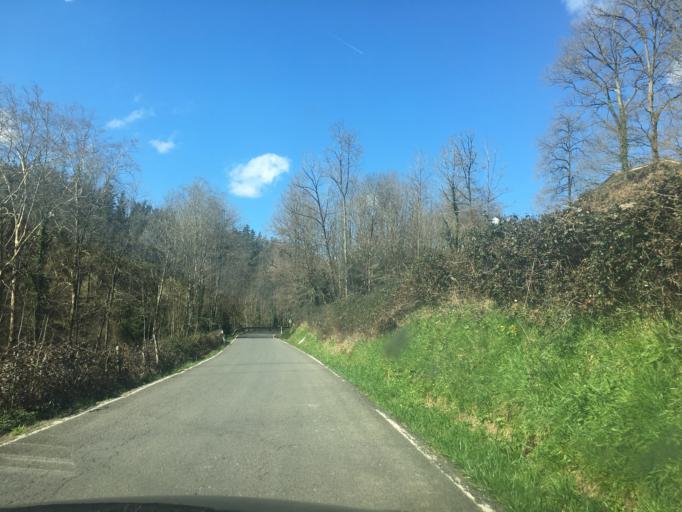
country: ES
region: Basque Country
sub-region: Bizkaia
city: Amorebieta
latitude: 43.2393
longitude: -2.7426
